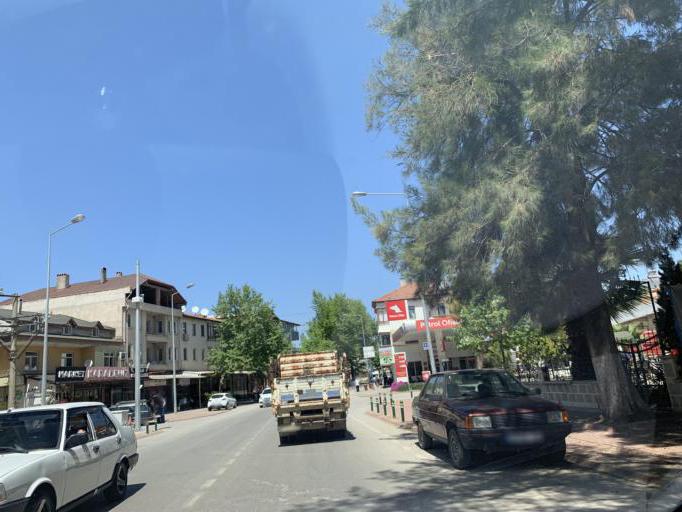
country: TR
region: Bursa
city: Iznik
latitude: 40.4240
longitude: 29.7195
